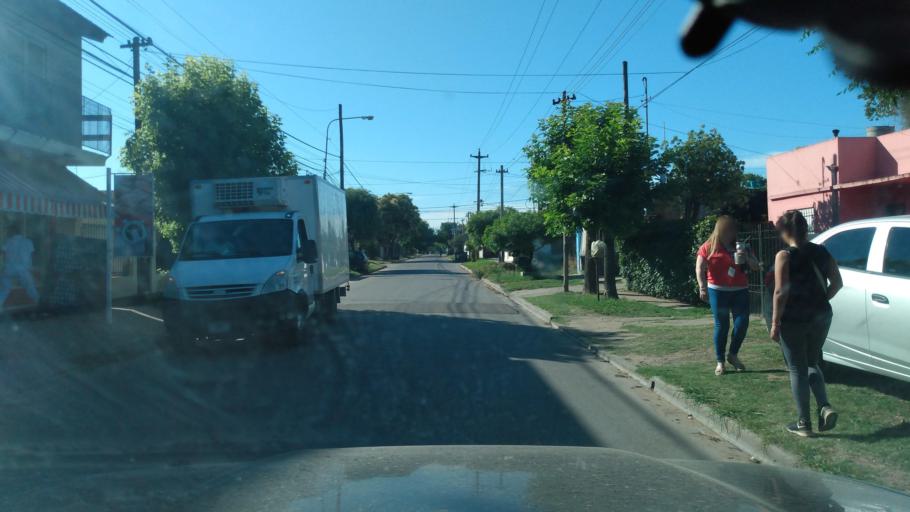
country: AR
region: Buenos Aires
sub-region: Partido de Lujan
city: Lujan
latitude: -34.5703
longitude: -59.0900
